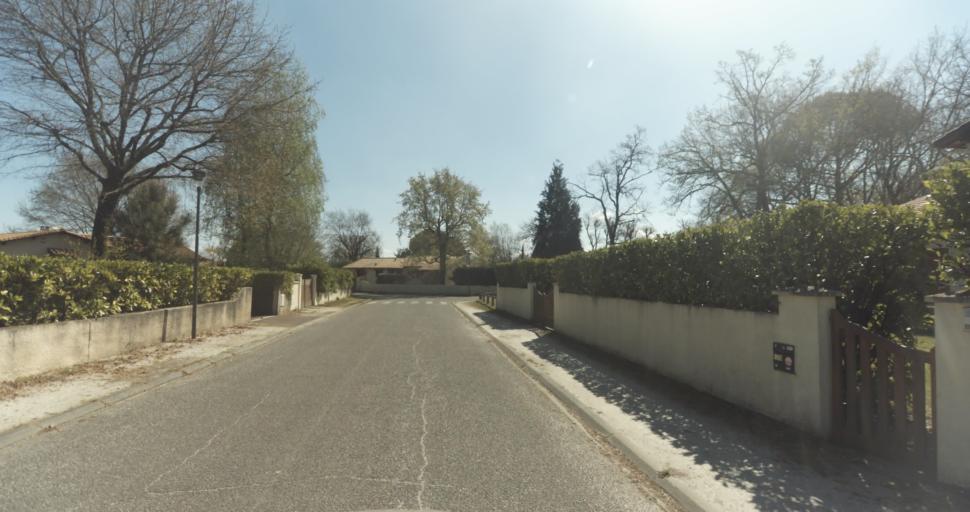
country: FR
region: Aquitaine
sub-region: Departement de la Gironde
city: Martignas-sur-Jalle
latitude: 44.8063
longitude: -0.7880
